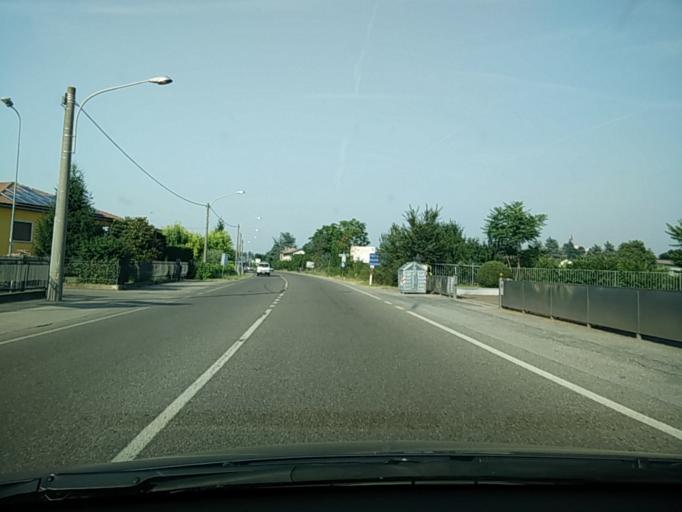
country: IT
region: Lombardy
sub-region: Provincia di Pavia
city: Montebello
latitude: 45.0090
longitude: 9.1120
